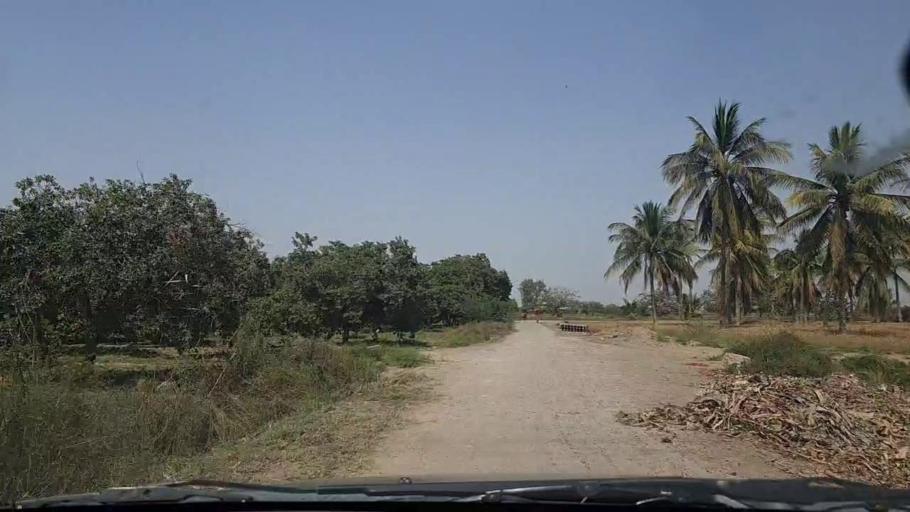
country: PK
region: Sindh
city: Keti Bandar
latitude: 24.2835
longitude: 67.6730
